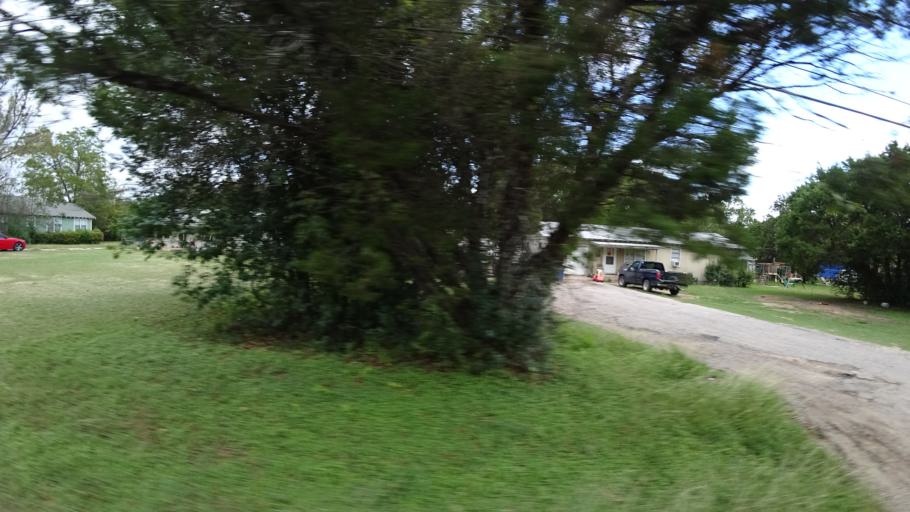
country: US
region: Texas
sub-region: Travis County
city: Onion Creek
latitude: 30.1884
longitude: -97.7941
